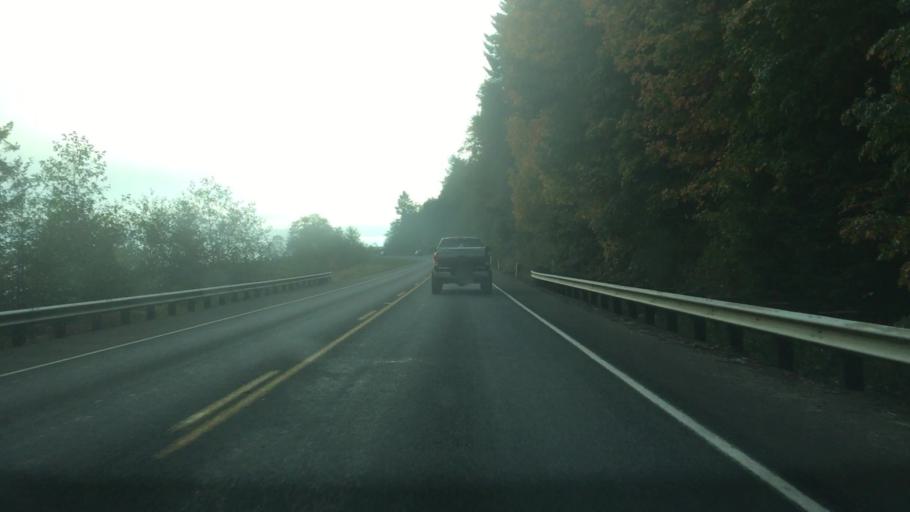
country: US
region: Oregon
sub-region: Clatsop County
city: Astoria
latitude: 46.2756
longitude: -123.8156
